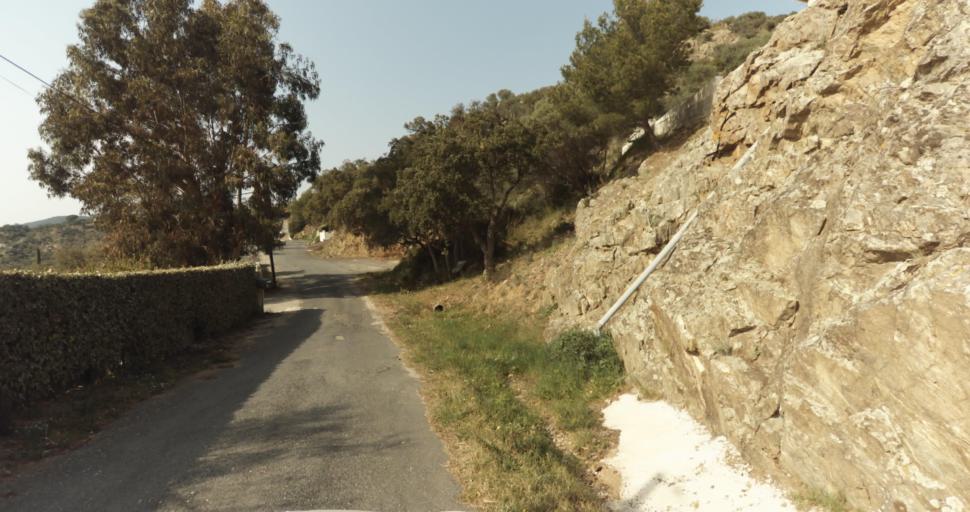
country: FR
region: Provence-Alpes-Cote d'Azur
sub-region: Departement du Var
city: Bormes-les-Mimosas
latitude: 43.1474
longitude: 6.3290
